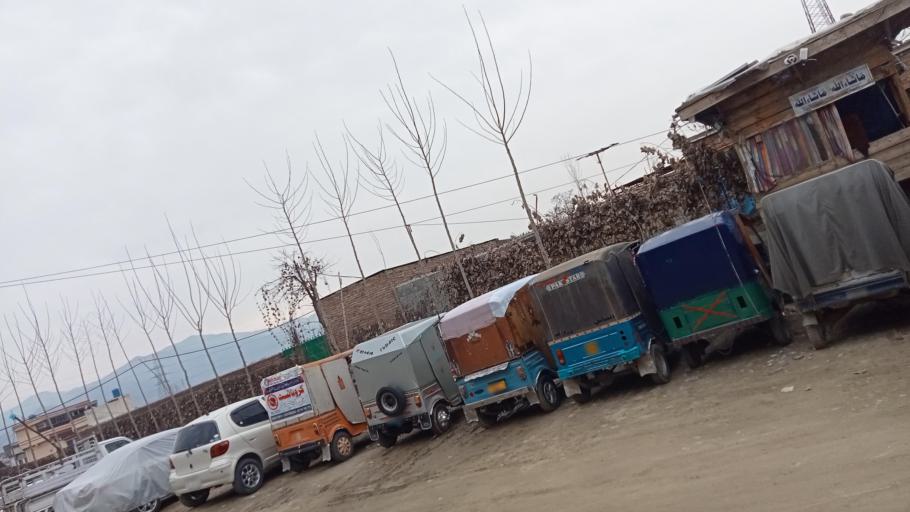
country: PK
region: Khyber Pakhtunkhwa
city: Mingora
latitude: 34.7711
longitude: 72.3441
